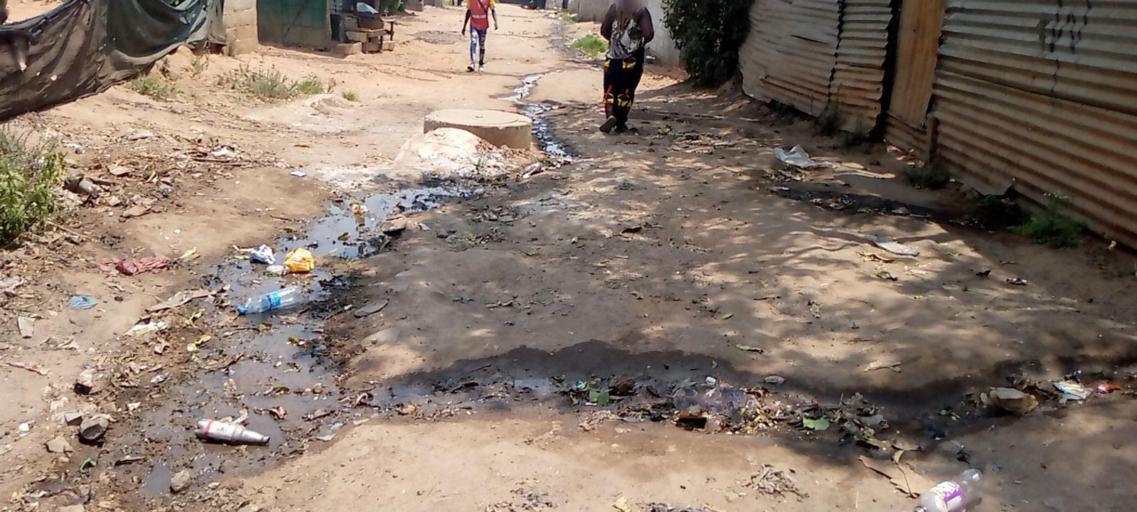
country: ZM
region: Lusaka
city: Lusaka
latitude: -15.3989
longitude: 28.3490
